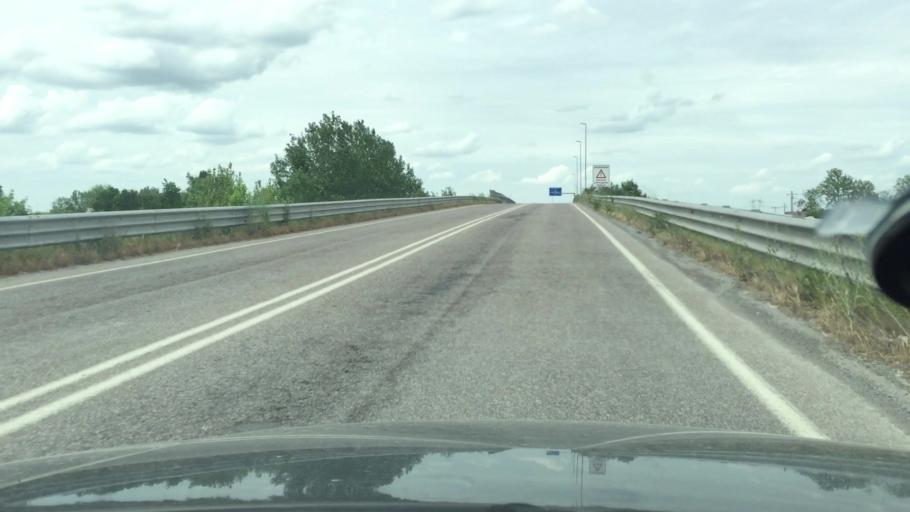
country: IT
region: Emilia-Romagna
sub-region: Provincia di Ferrara
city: Cona
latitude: 44.8014
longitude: 11.7216
